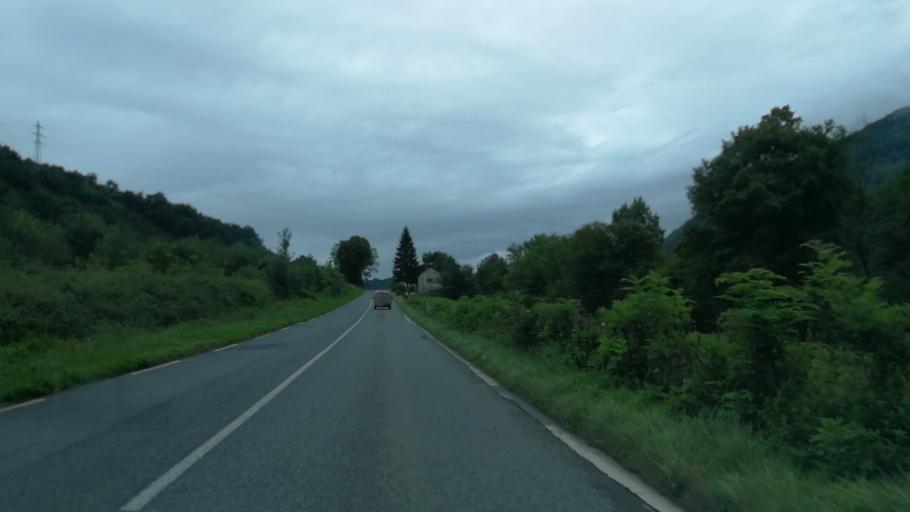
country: FR
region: Aquitaine
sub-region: Departement des Pyrenees-Atlantiques
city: Oloron-Sainte-Marie
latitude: 43.1125
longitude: -0.6229
